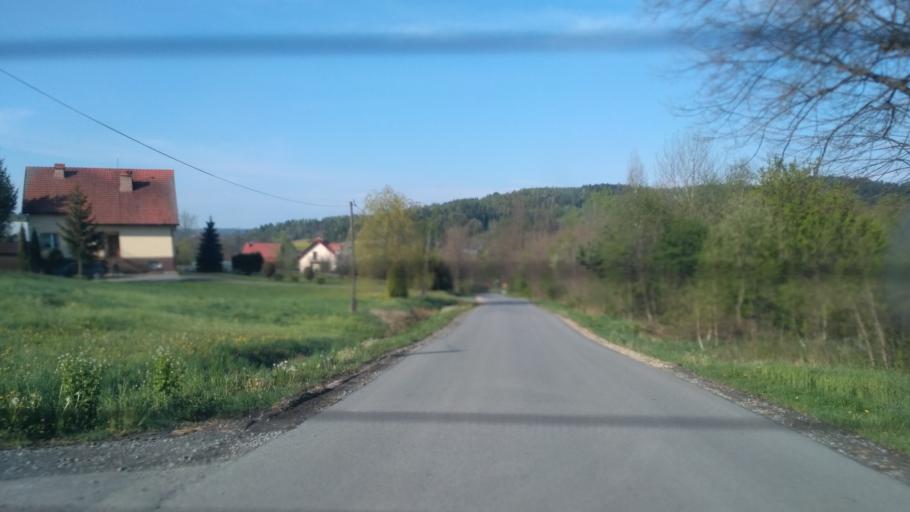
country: PL
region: Subcarpathian Voivodeship
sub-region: Powiat jaroslawski
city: Kramarzowka
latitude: 49.8292
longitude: 22.5037
